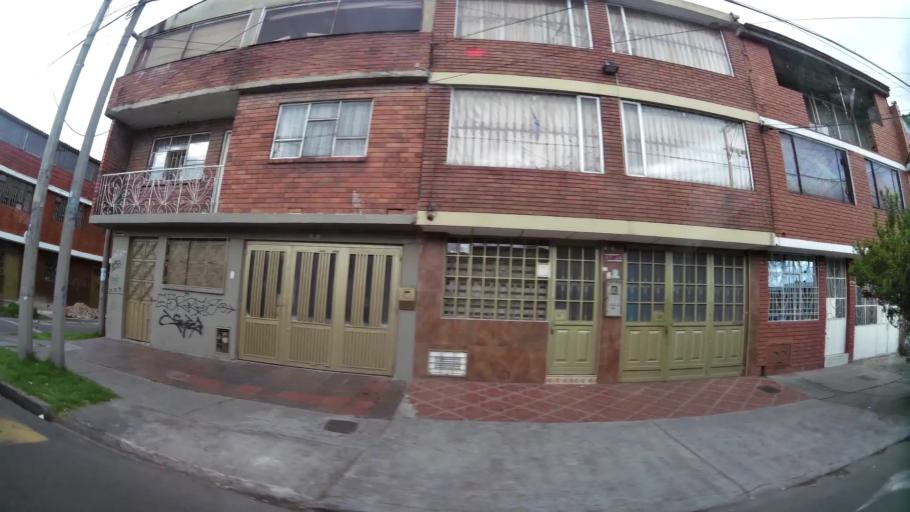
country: CO
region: Bogota D.C.
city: Bogota
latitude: 4.6099
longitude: -74.1146
